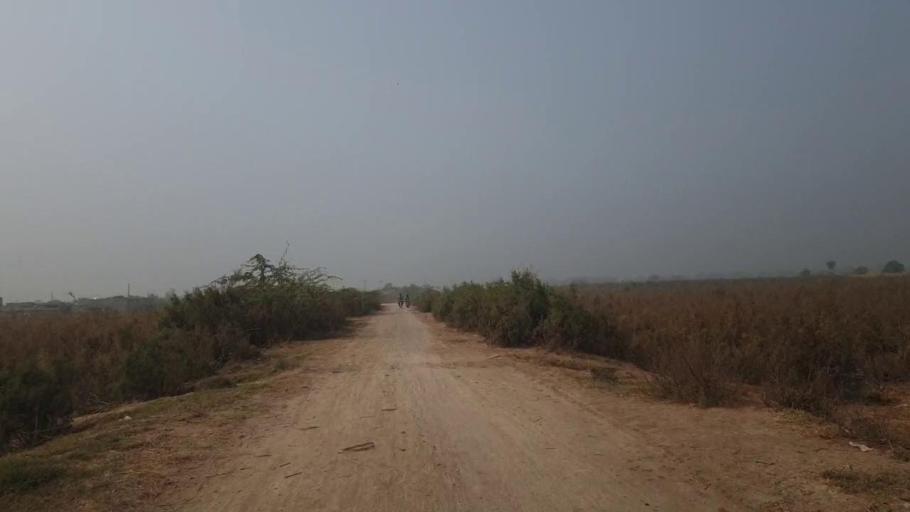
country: PK
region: Sindh
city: Bhit Shah
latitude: 25.7886
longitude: 68.5554
